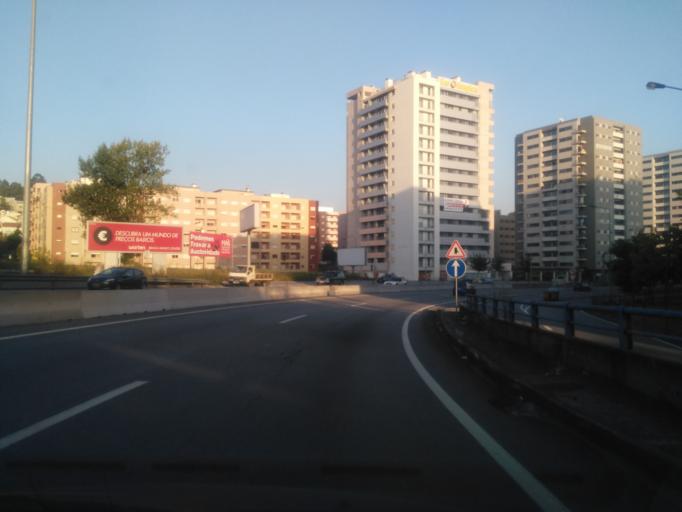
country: PT
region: Braga
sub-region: Braga
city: Braga
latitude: 41.5624
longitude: -8.4085
